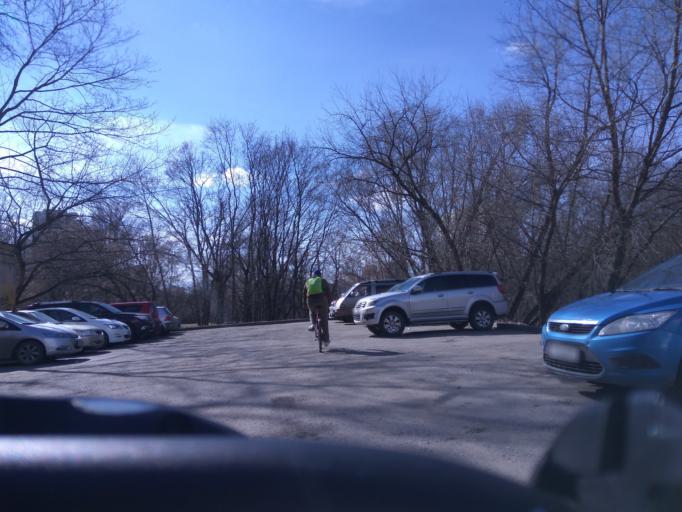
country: RU
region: Moskovskaya
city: Fili
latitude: 55.7368
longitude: 37.4752
